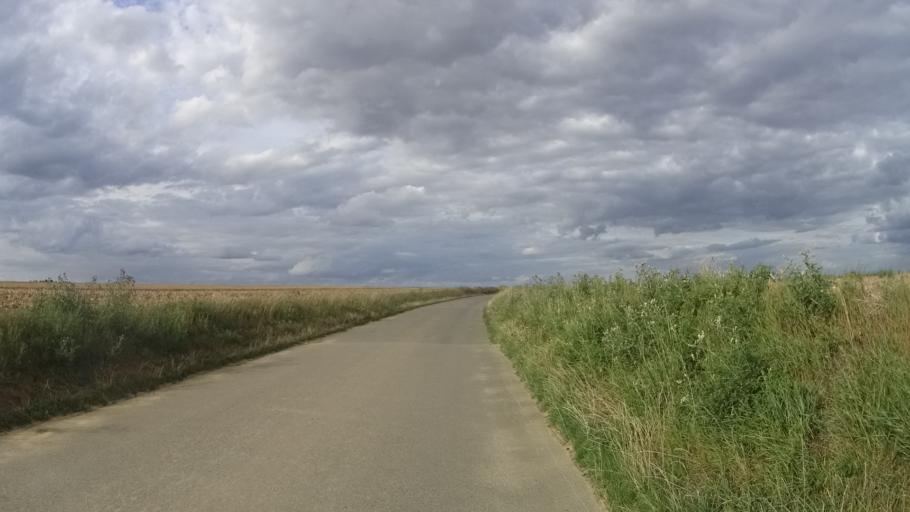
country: FR
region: Picardie
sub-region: Departement de l'Oise
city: Ver-sur-Launette
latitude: 49.0955
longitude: 2.7115
